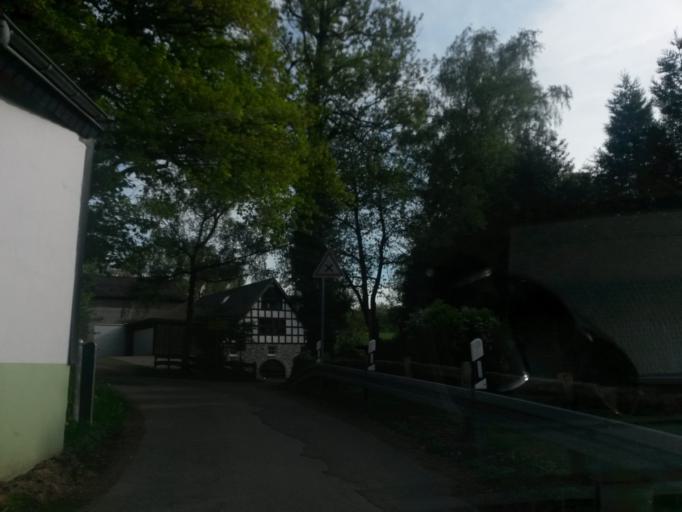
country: DE
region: North Rhine-Westphalia
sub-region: Regierungsbezirk Arnsberg
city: Schalksmuhle
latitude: 51.2951
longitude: 7.5505
